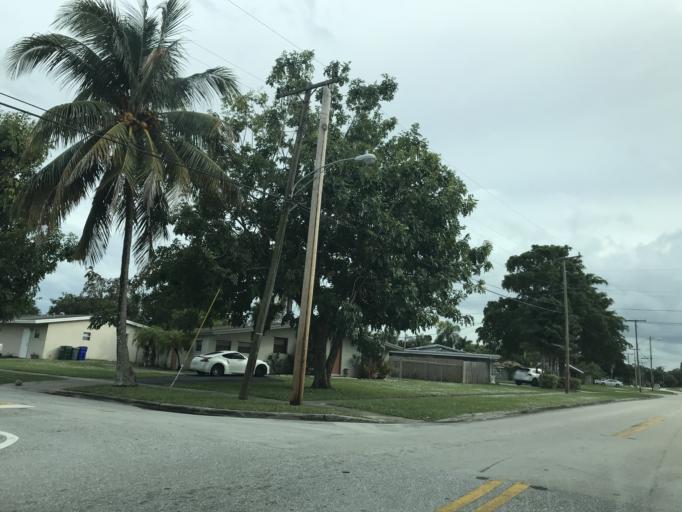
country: US
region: Florida
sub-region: Broward County
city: Margate
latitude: 26.2546
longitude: -80.2061
